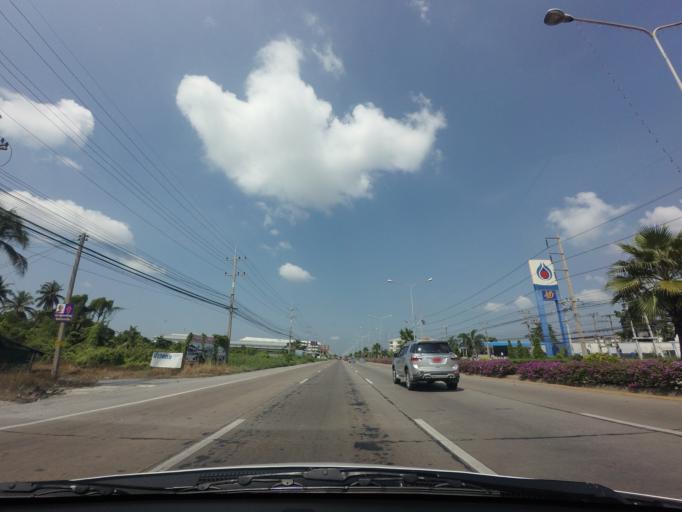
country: TH
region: Nakhon Pathom
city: Sam Phran
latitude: 13.7472
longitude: 100.2045
